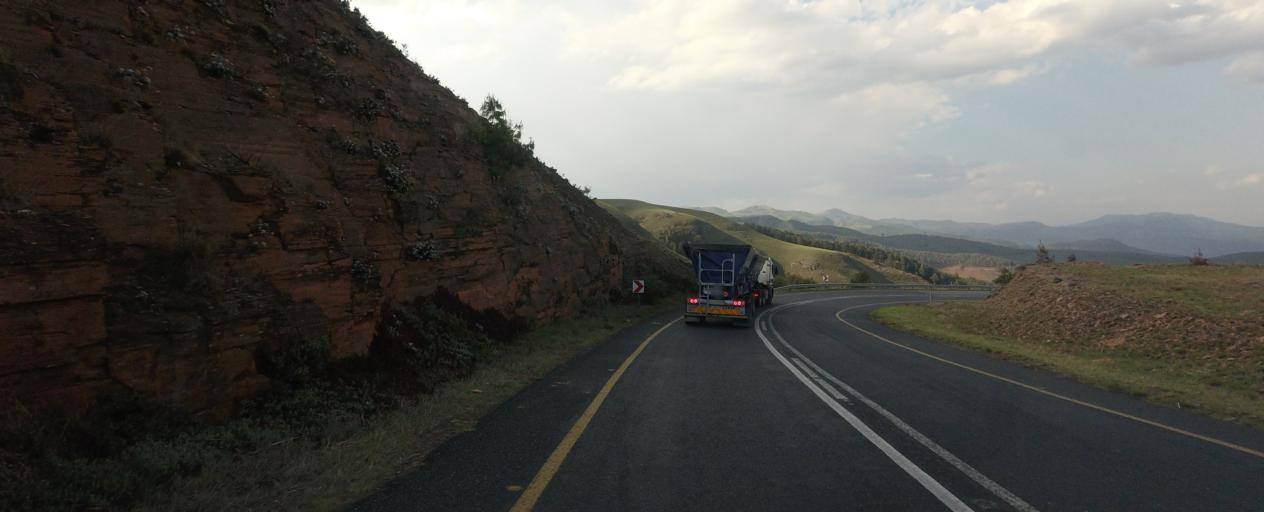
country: ZA
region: Mpumalanga
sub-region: Ehlanzeni District
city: Lydenburg
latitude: -25.1572
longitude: 30.6274
